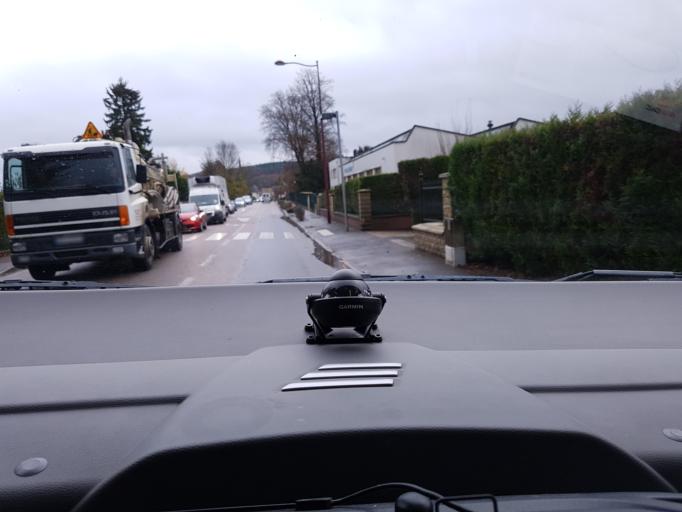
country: FR
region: Haute-Normandie
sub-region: Departement de l'Eure
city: Pont-Saint-Pierre
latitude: 49.3361
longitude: 1.2687
